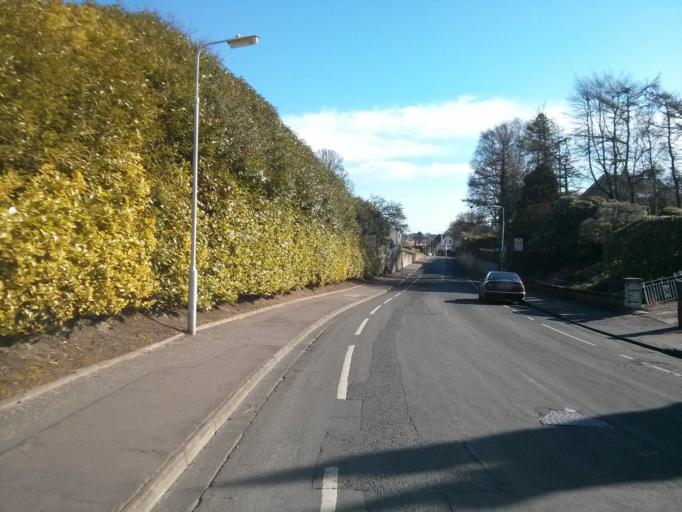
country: GB
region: Scotland
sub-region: Fife
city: Saint Andrews
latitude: 56.3344
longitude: -2.8054
